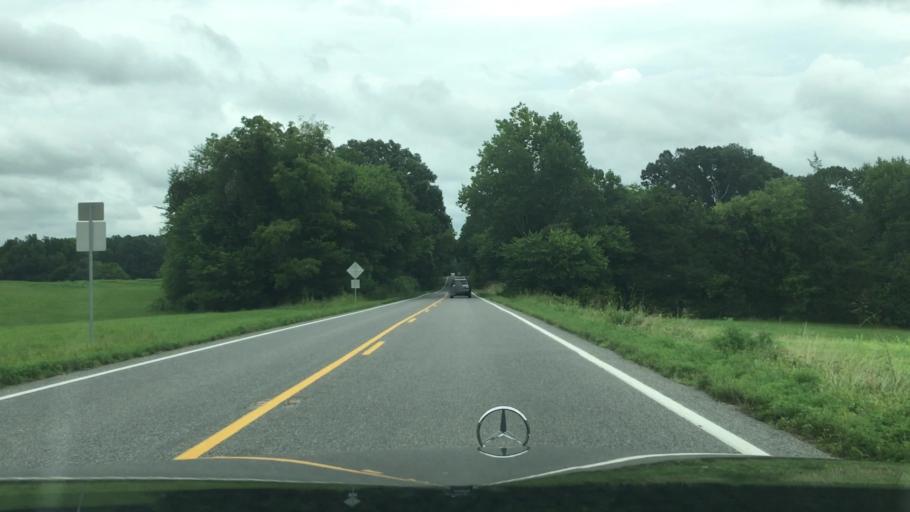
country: US
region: Virginia
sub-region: Nottoway County
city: Crewe
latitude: 37.2728
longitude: -78.1604
